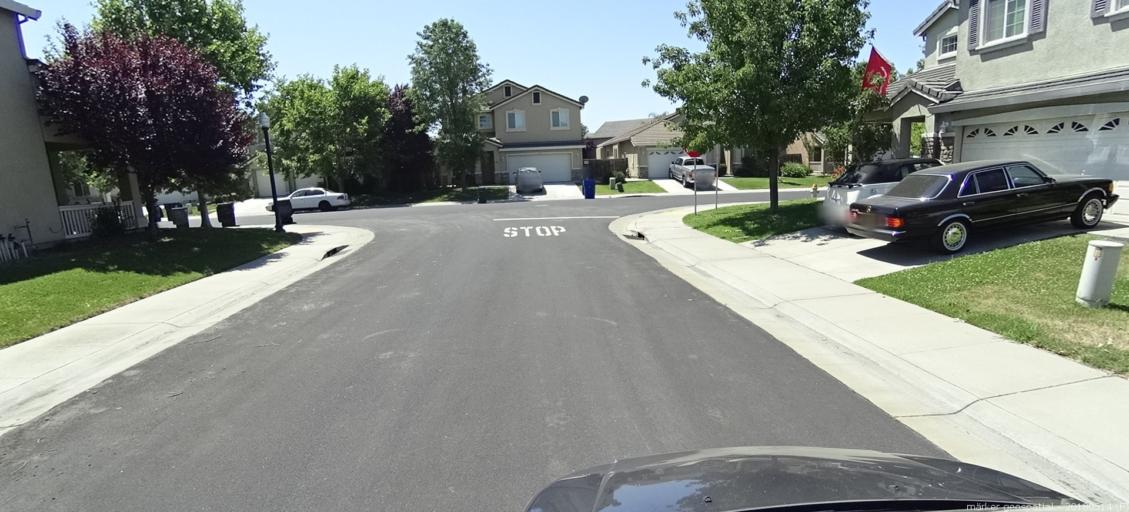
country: US
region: California
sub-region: Yolo County
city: West Sacramento
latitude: 38.6325
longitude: -121.5302
